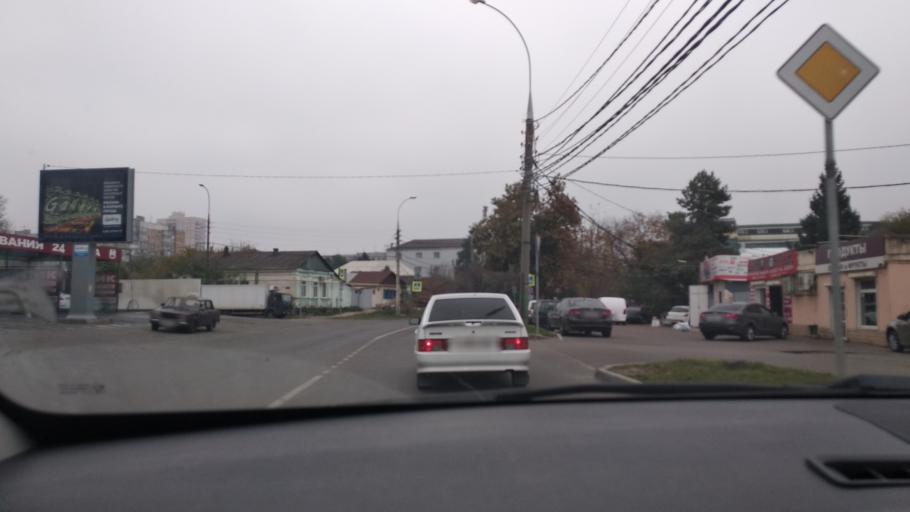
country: RU
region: Krasnodarskiy
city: Krasnodar
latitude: 45.0234
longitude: 39.0092
